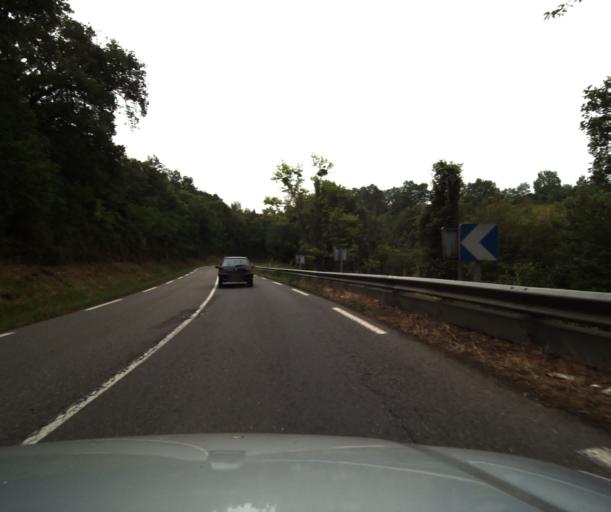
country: FR
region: Midi-Pyrenees
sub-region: Departement du Gers
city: Mielan
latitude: 43.4773
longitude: 0.3357
